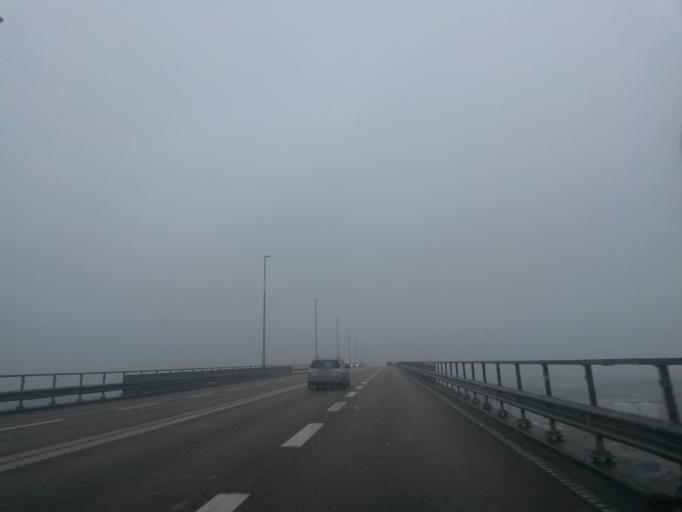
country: SE
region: Vaestra Goetaland
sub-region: Trollhattan
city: Trollhattan
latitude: 58.3073
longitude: 12.3207
